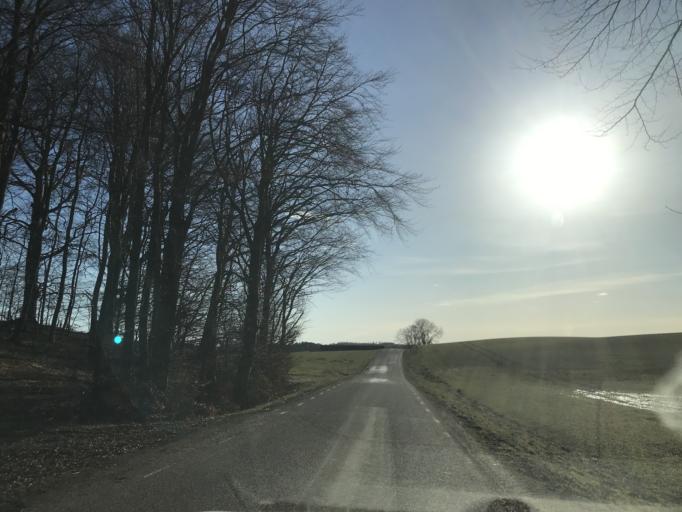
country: SE
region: Skane
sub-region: Ystads Kommun
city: Ystad
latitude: 55.5469
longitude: 13.7930
